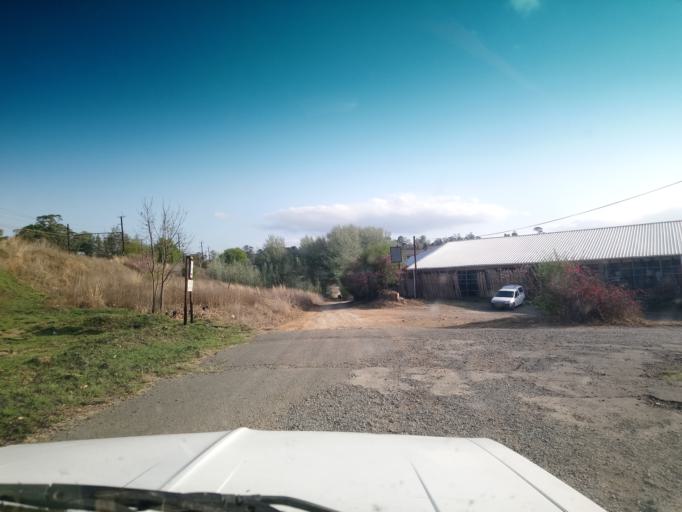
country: ZA
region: KwaZulu-Natal
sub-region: uMgungundlovu District Municipality
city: Mooirivier
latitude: -29.3069
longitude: 29.9775
